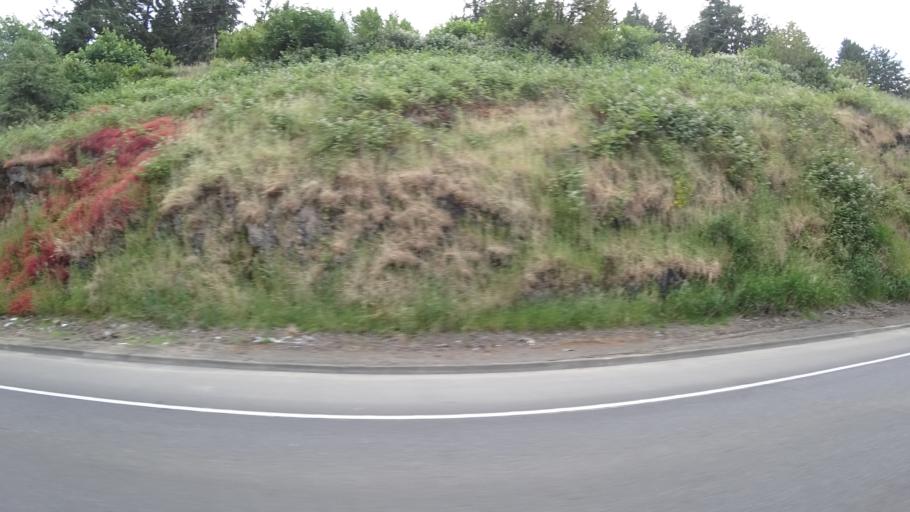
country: US
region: Oregon
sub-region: Washington County
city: Bethany
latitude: 45.6246
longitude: -122.8158
